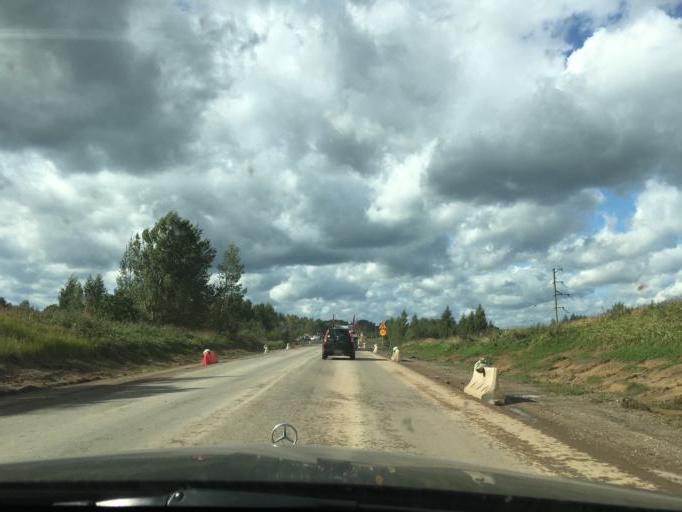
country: RU
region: Pskov
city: Novosokol'niki
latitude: 56.2834
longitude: 30.2760
